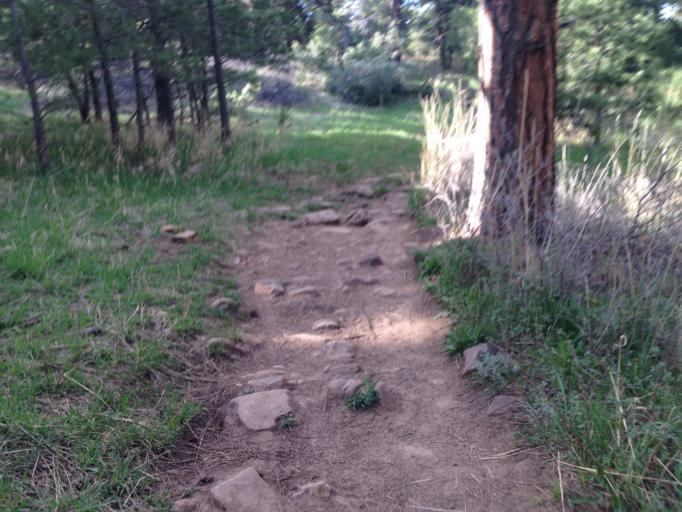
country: US
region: Colorado
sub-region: Boulder County
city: Boulder
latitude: 39.9470
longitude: -105.2796
